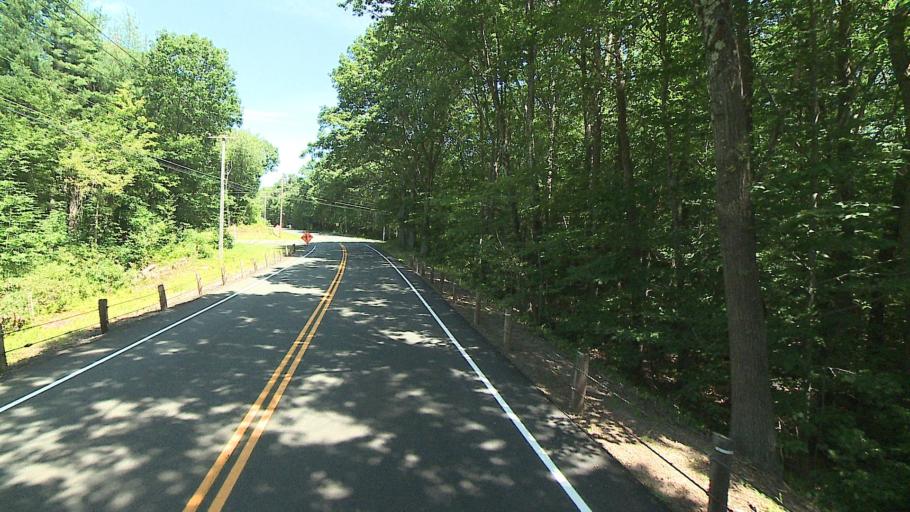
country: US
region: Connecticut
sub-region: Hartford County
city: North Granby
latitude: 41.9861
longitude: -72.9118
